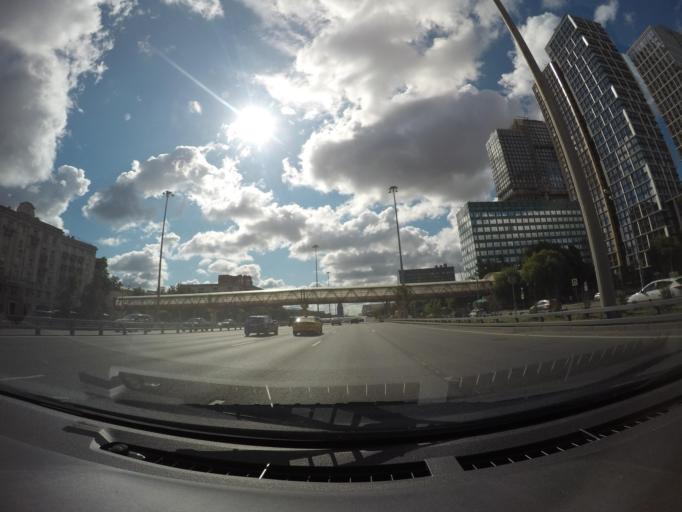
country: RU
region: Moscow
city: Sokol
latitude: 55.7958
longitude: 37.5420
